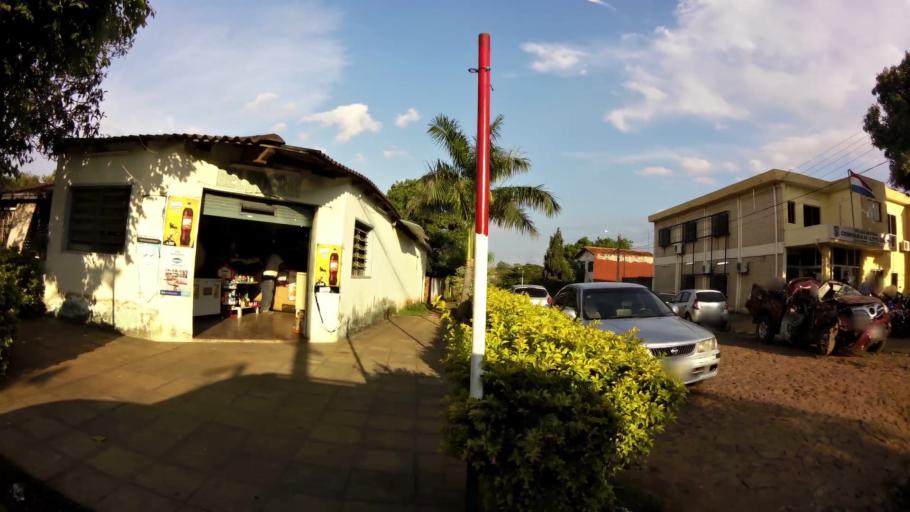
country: PY
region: Central
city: Fernando de la Mora
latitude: -25.3612
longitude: -57.5296
